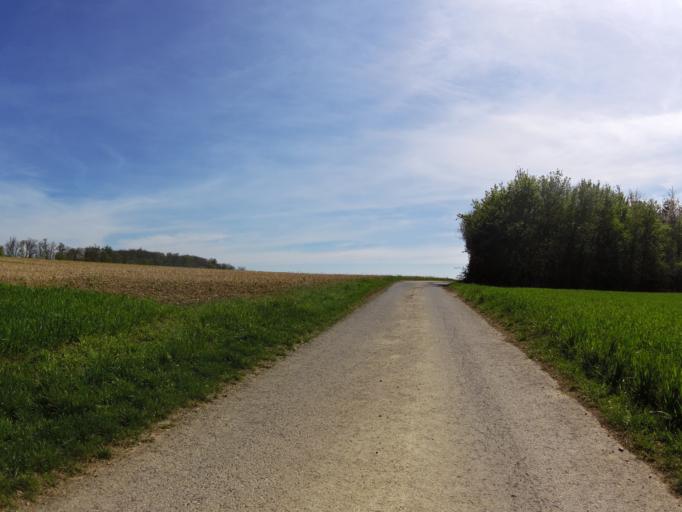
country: DE
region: Bavaria
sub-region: Regierungsbezirk Unterfranken
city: Rimpar
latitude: 49.8611
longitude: 9.9751
